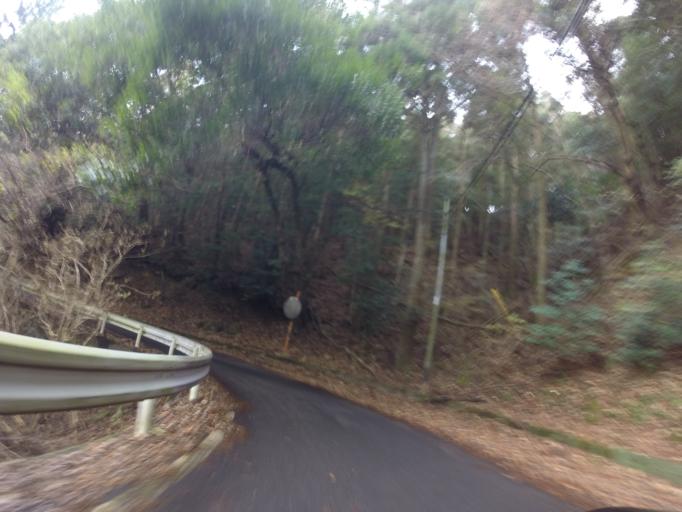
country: JP
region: Shizuoka
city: Heda
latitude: 34.8752
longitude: 138.8588
